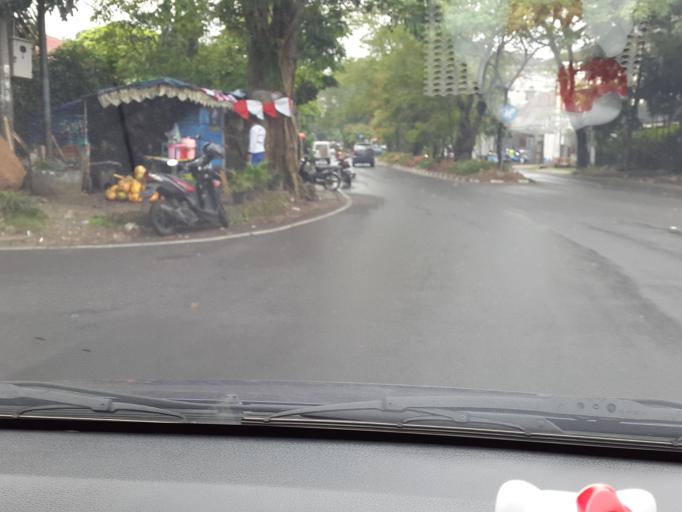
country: ID
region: West Java
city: Bandung
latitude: -6.9051
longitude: 107.6269
